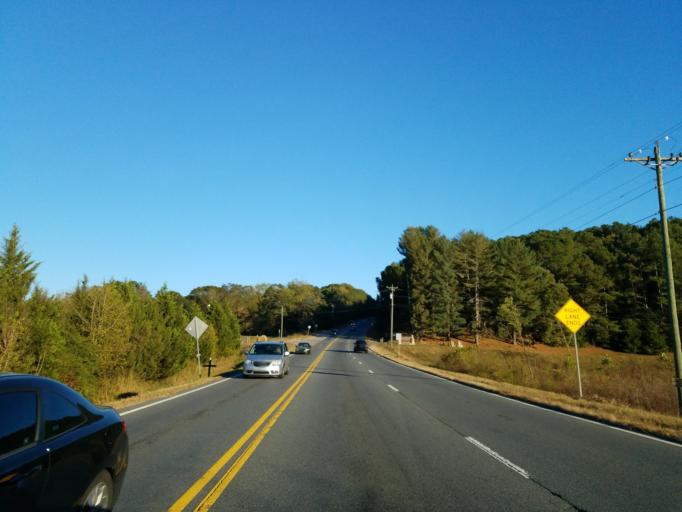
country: US
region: Georgia
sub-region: Dawson County
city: Dawsonville
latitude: 34.3814
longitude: -84.0616
